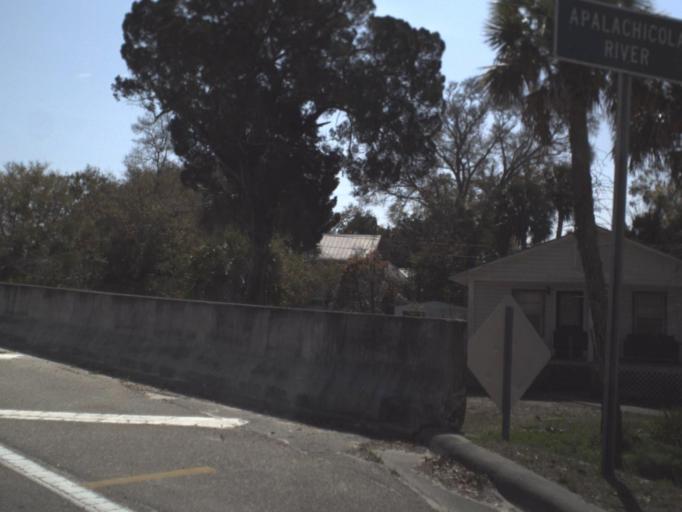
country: US
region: Florida
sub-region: Franklin County
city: Apalachicola
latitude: 29.7254
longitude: -84.9831
